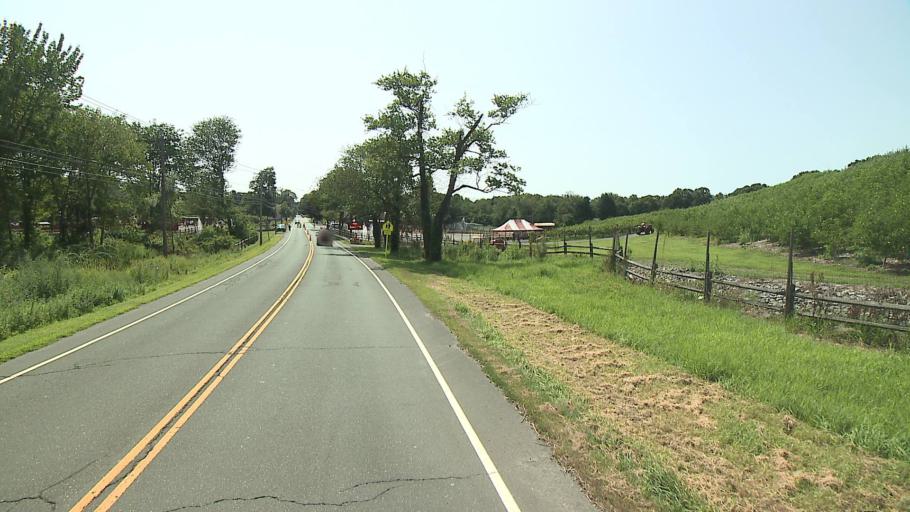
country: US
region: Connecticut
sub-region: Fairfield County
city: Trumbull
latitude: 41.2512
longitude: -73.2802
